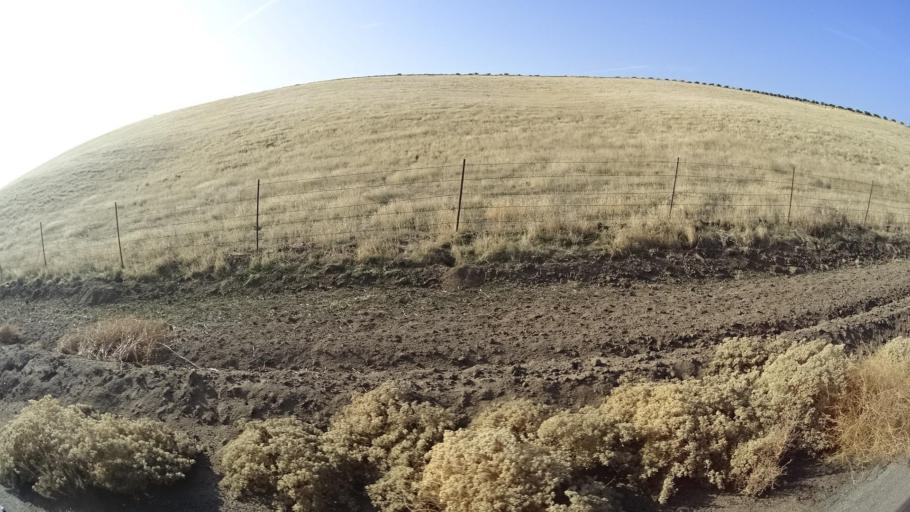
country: US
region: California
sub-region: Tulare County
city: Richgrove
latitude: 35.6419
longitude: -119.0473
